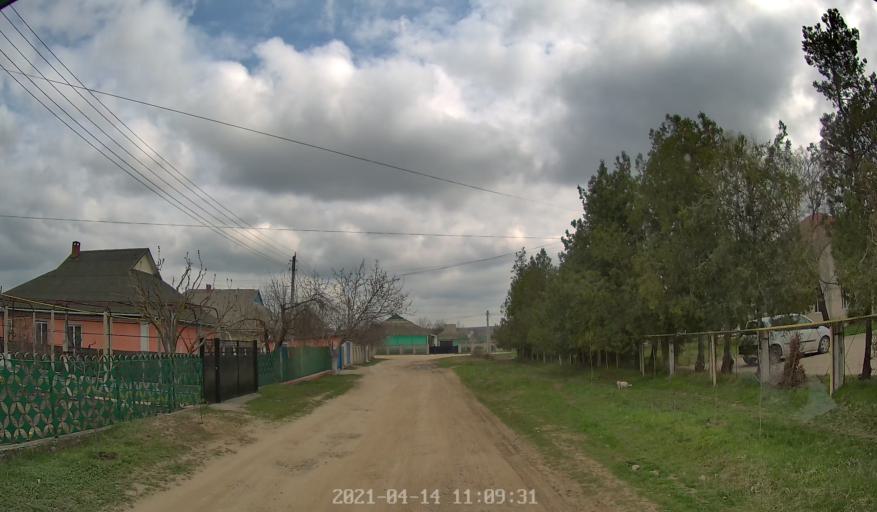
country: MD
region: Criuleni
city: Criuleni
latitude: 47.1561
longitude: 29.1466
